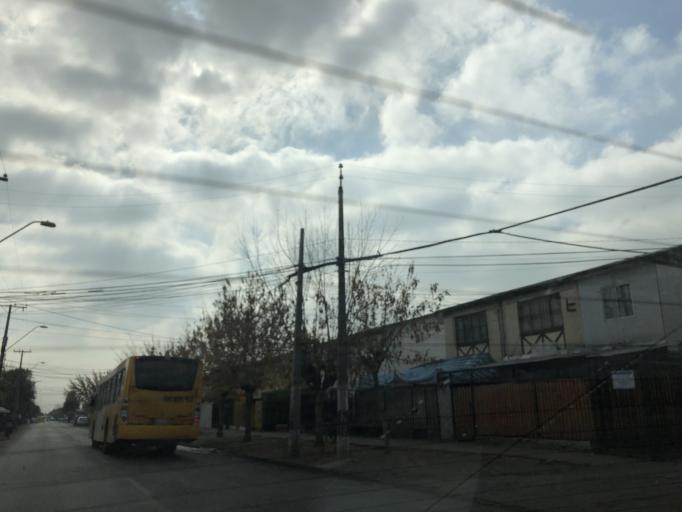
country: CL
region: Santiago Metropolitan
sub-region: Provincia de Cordillera
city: Puente Alto
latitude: -33.5854
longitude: -70.5915
